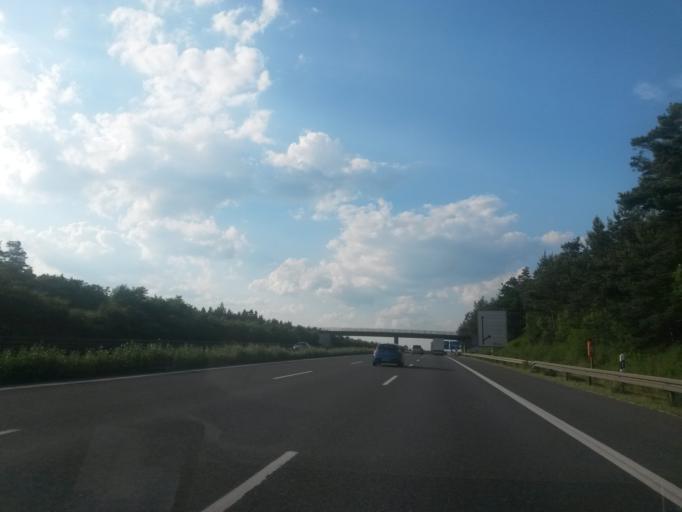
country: DE
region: Bavaria
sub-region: Regierungsbezirk Mittelfranken
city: Feucht
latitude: 49.3379
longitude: 11.2044
